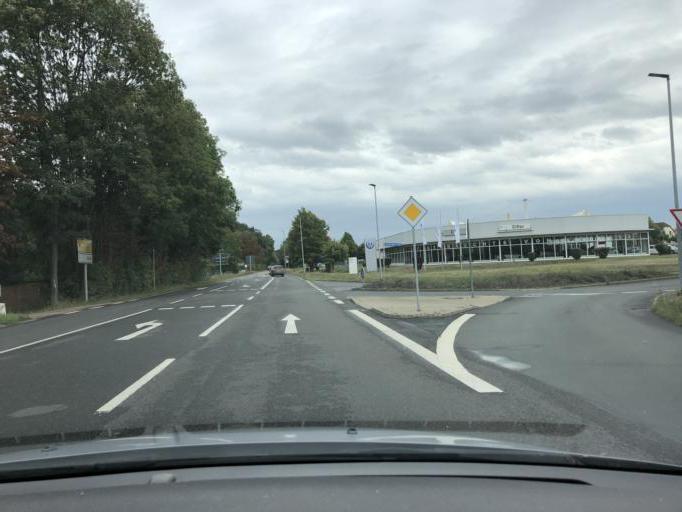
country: DE
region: Saxony-Anhalt
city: Koethen
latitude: 51.7559
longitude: 11.9453
